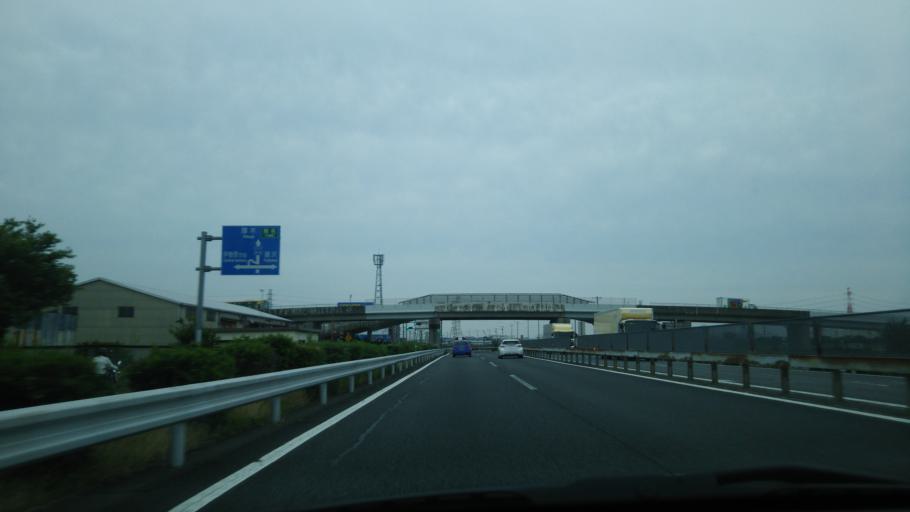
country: JP
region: Kanagawa
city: Isehara
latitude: 35.3898
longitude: 139.3327
